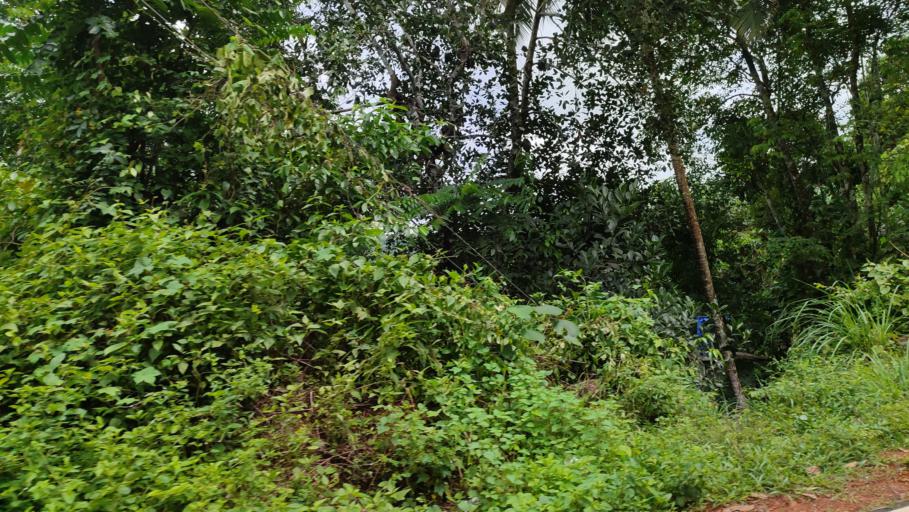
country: IN
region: Kerala
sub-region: Kasaragod District
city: Nileshwar
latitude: 12.2839
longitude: 75.2641
